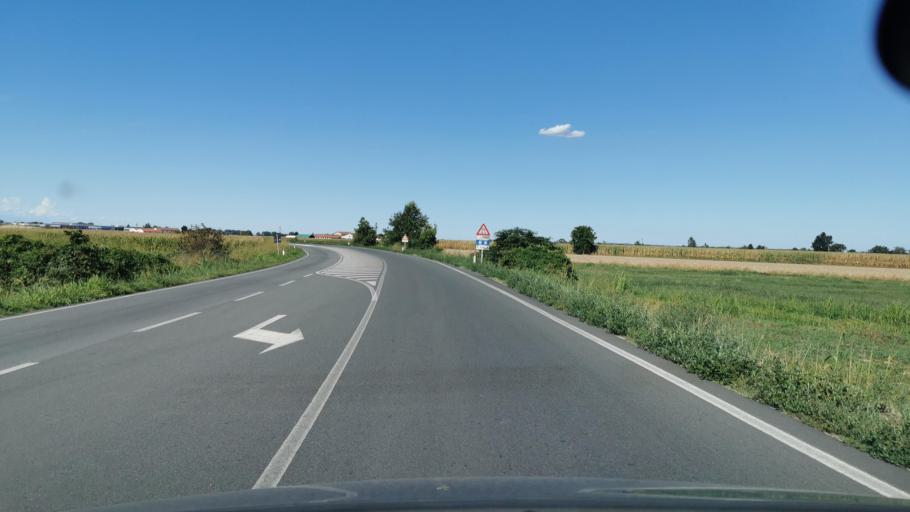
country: IT
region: Piedmont
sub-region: Provincia di Cuneo
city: Savigliano
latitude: 44.6414
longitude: 7.6731
